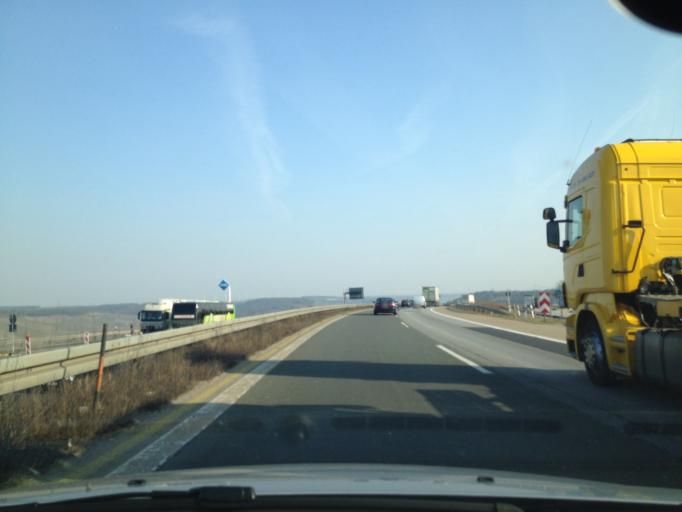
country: DE
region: Bavaria
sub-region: Regierungsbezirk Unterfranken
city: Randersacker
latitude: 49.7540
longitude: 9.9614
